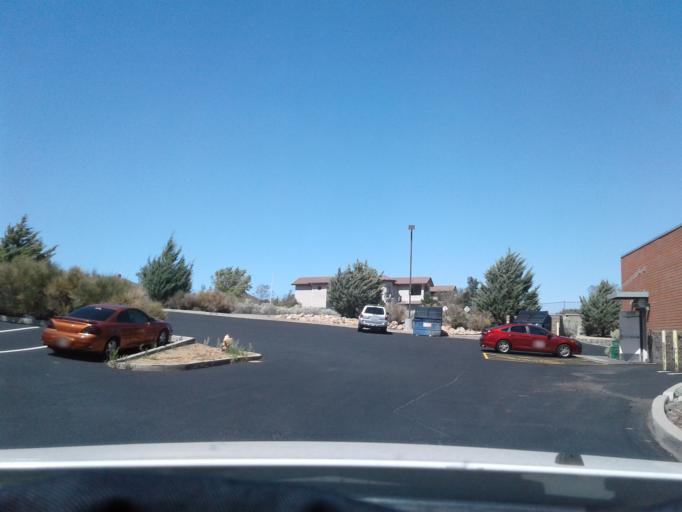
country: US
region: Arizona
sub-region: Yavapai County
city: Prescott
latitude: 34.5740
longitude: -112.4459
